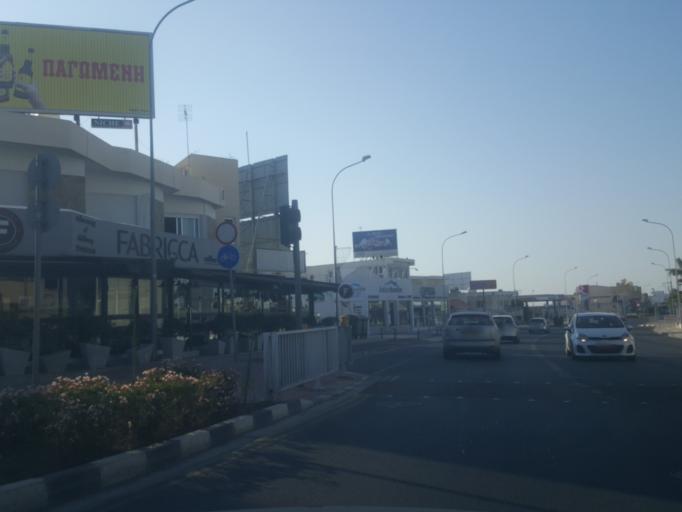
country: CY
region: Ammochostos
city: Paralimni
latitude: 35.0343
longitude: 33.9786
